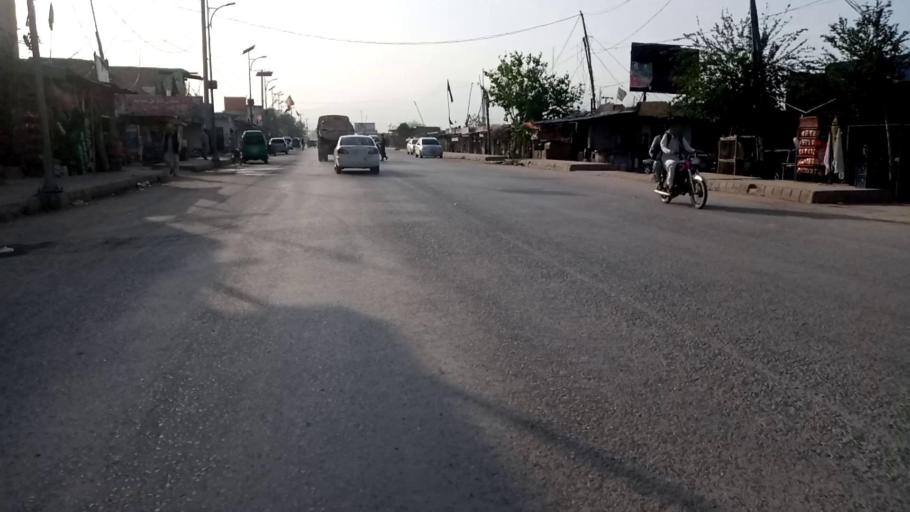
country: PK
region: Khyber Pakhtunkhwa
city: Peshawar
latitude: 33.9989
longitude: 71.4176
